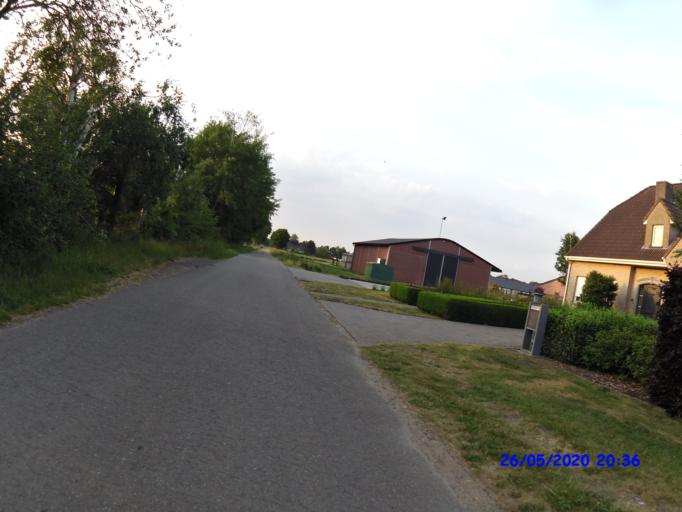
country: BE
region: Flanders
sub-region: Provincie Antwerpen
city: Geel
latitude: 51.1861
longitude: 5.0015
